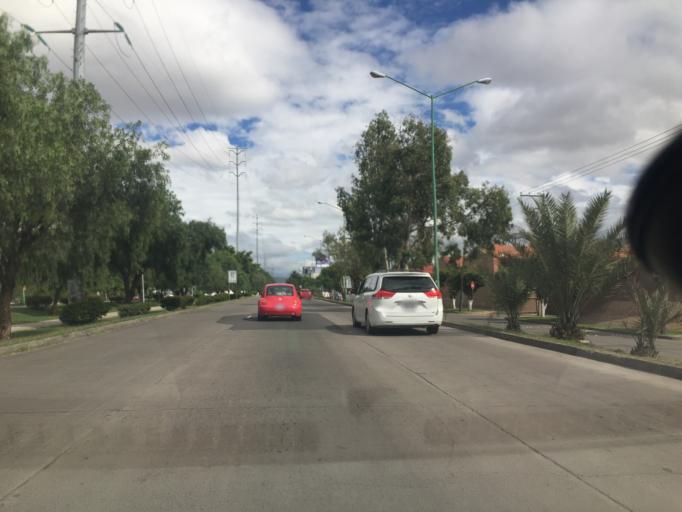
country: MX
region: Guanajuato
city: Leon
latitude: 21.1536
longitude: -101.6799
